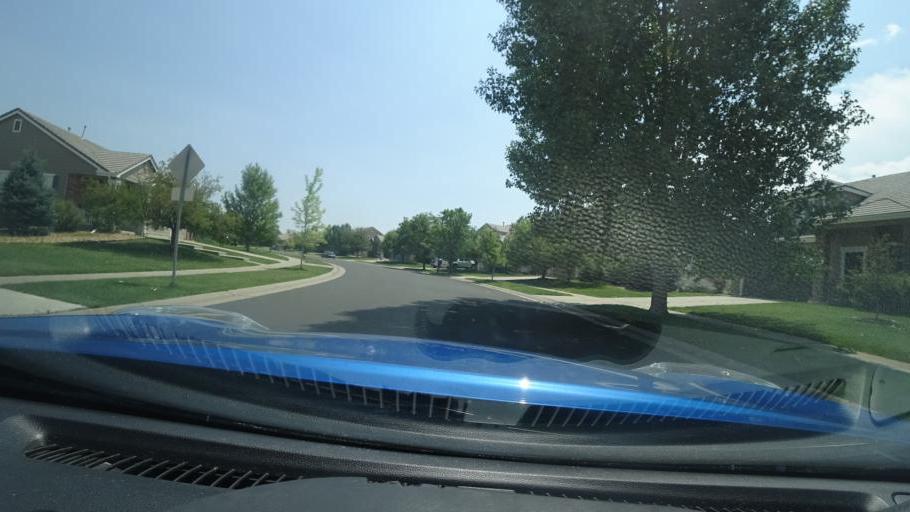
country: US
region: Colorado
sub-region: Adams County
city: Aurora
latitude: 39.6719
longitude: -104.7705
